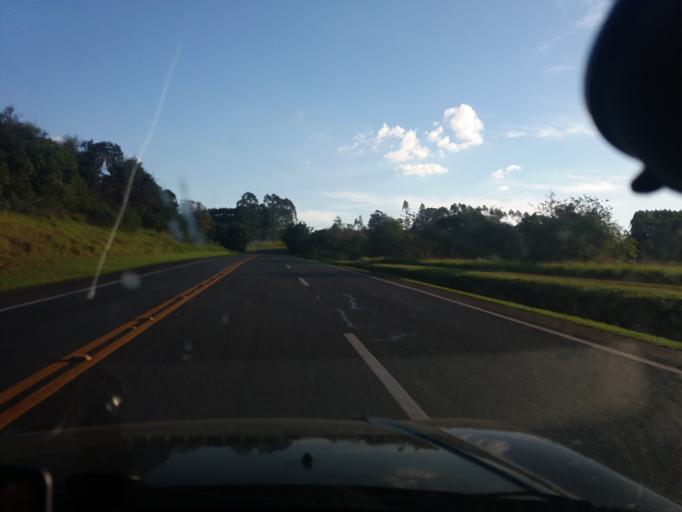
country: BR
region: Sao Paulo
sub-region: Buri
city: Buri
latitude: -23.9277
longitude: -48.6631
